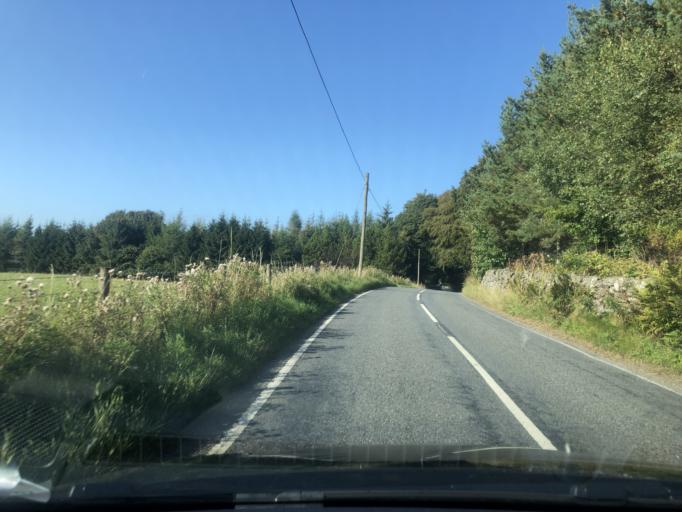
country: GB
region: Scotland
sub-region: Perth and Kinross
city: Blairgowrie
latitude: 56.6810
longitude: -3.4703
